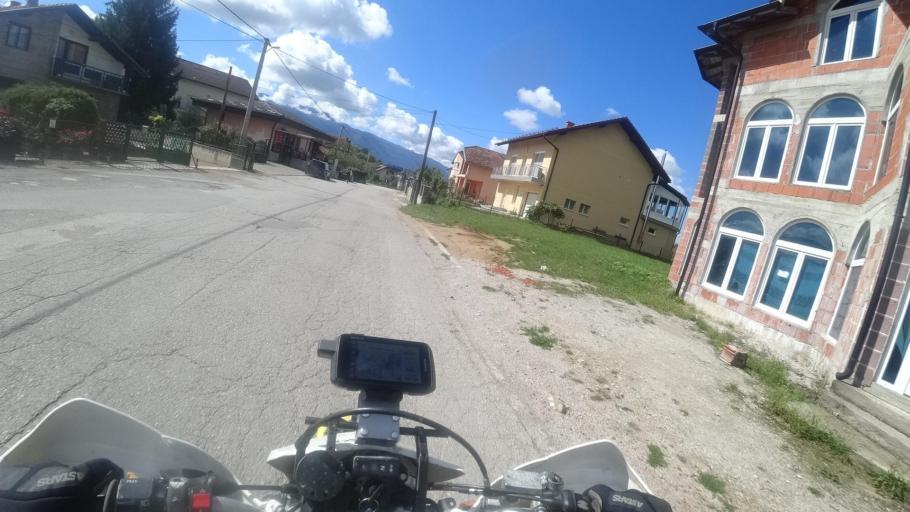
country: BA
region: Federation of Bosnia and Herzegovina
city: Bihac
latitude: 44.8134
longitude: 15.9002
